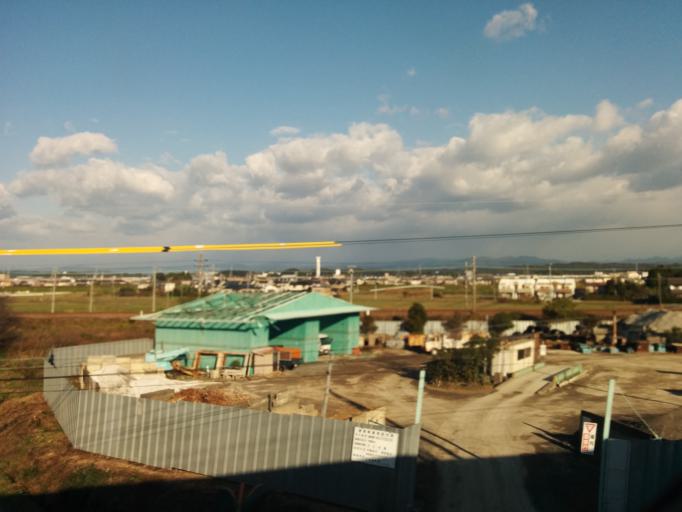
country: JP
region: Shizuoka
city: Fukuroi
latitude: 34.7438
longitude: 137.9373
